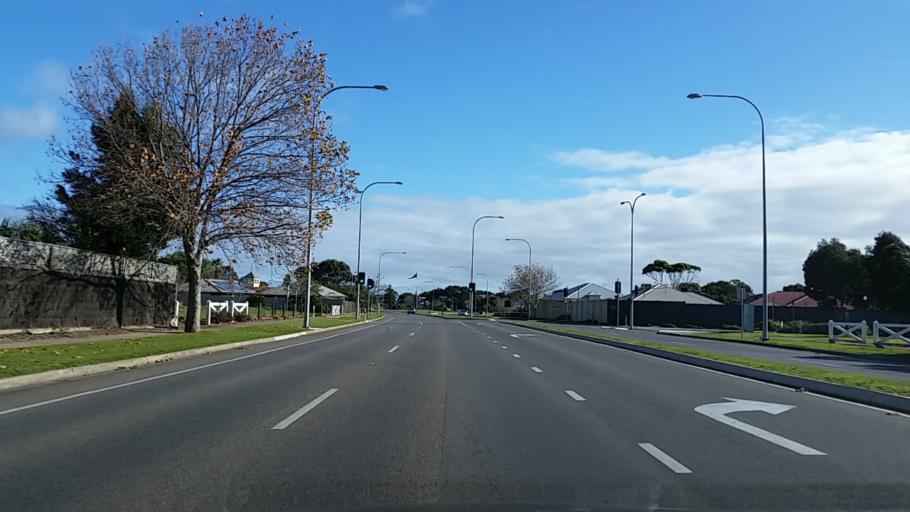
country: AU
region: South Australia
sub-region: Onkaparinga
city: Moana
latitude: -35.1914
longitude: 138.4843
